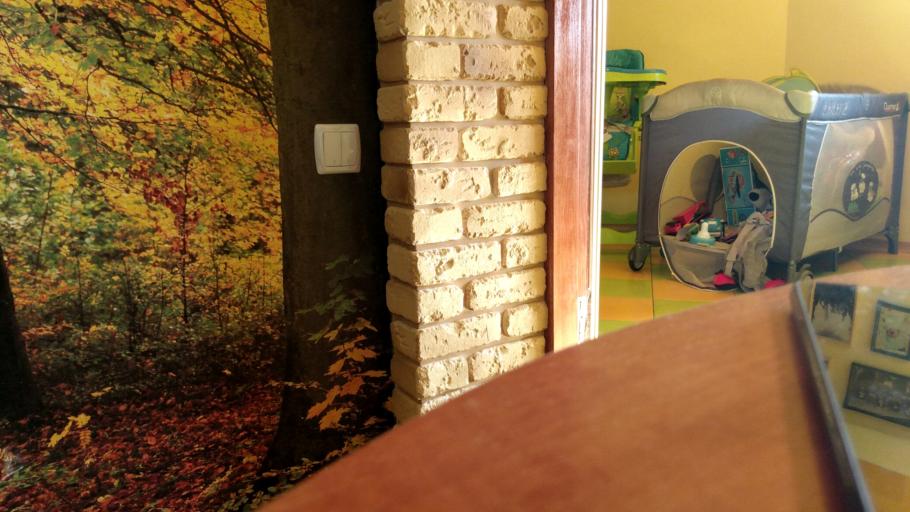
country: RU
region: Tverskaya
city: Gorodnya
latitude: 56.7403
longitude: 36.3478
